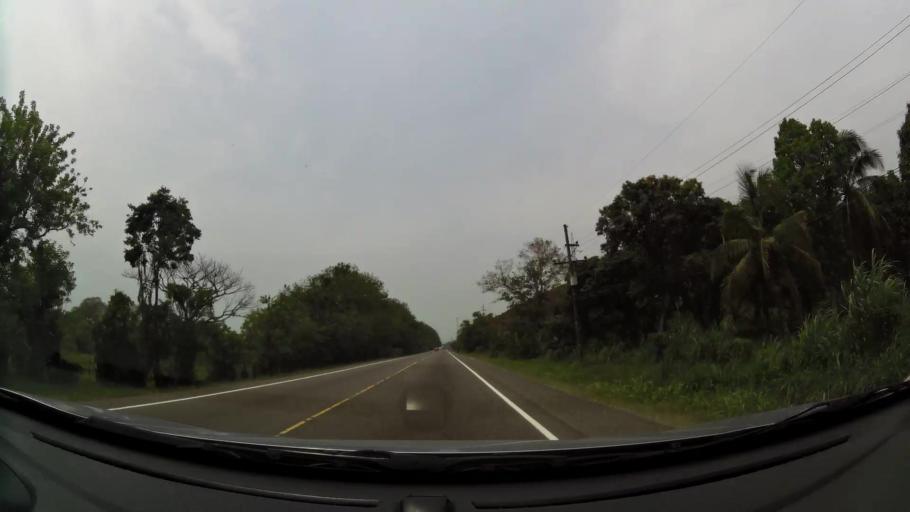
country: HN
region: Cortes
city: La Guama
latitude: 14.8340
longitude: -87.9601
